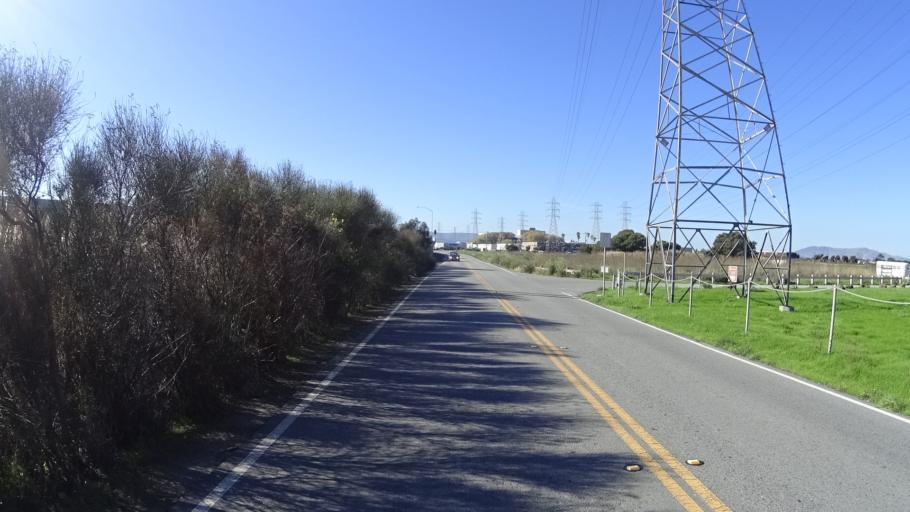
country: US
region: California
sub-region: San Mateo County
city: San Mateo
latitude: 37.5867
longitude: -122.3314
